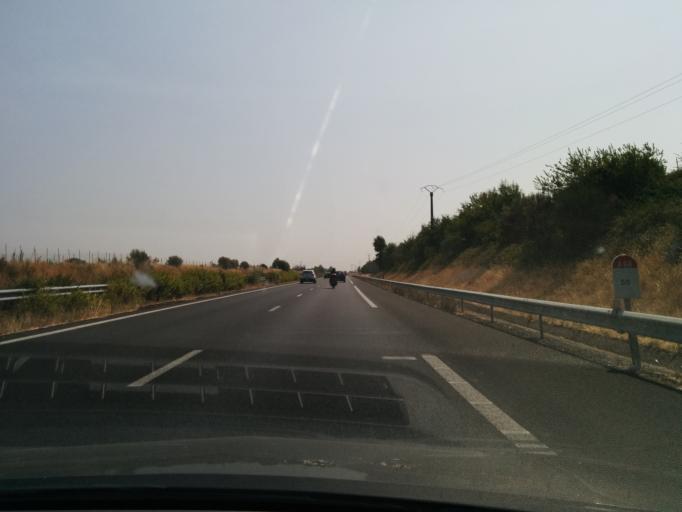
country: FR
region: Midi-Pyrenees
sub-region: Departement du Tarn
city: Brens
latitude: 43.8837
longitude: 1.9215
